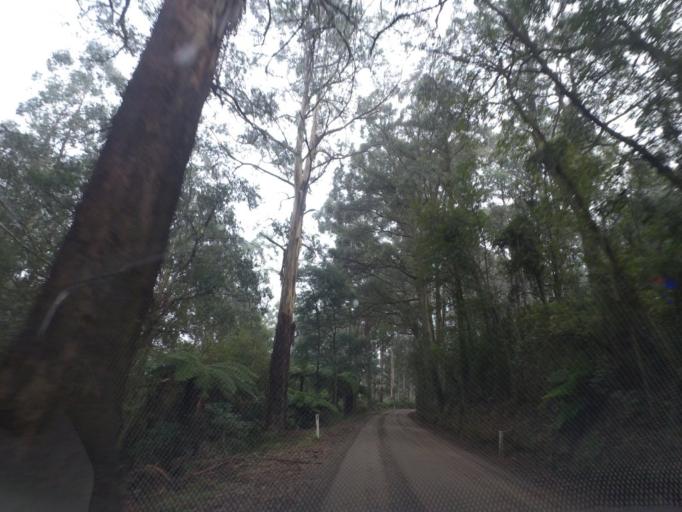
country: AU
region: Victoria
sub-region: Yarra Ranges
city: Badger Creek
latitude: -37.7067
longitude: 145.5817
